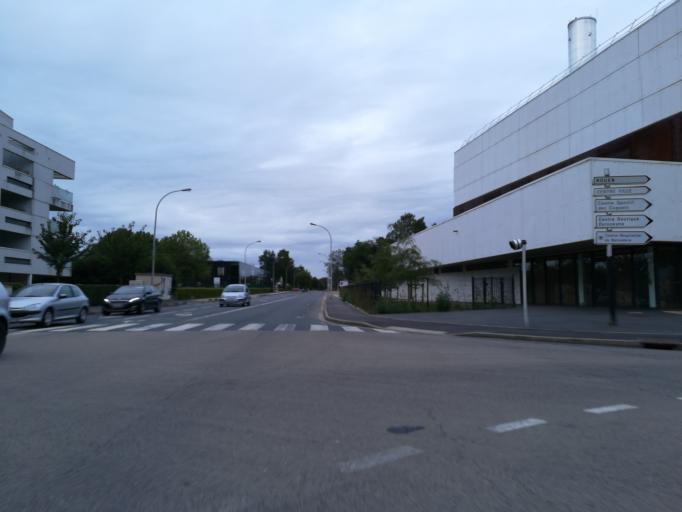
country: FR
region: Haute-Normandie
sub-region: Departement de la Seine-Maritime
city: Deville-les-Rouen
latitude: 49.4660
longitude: 1.0710
